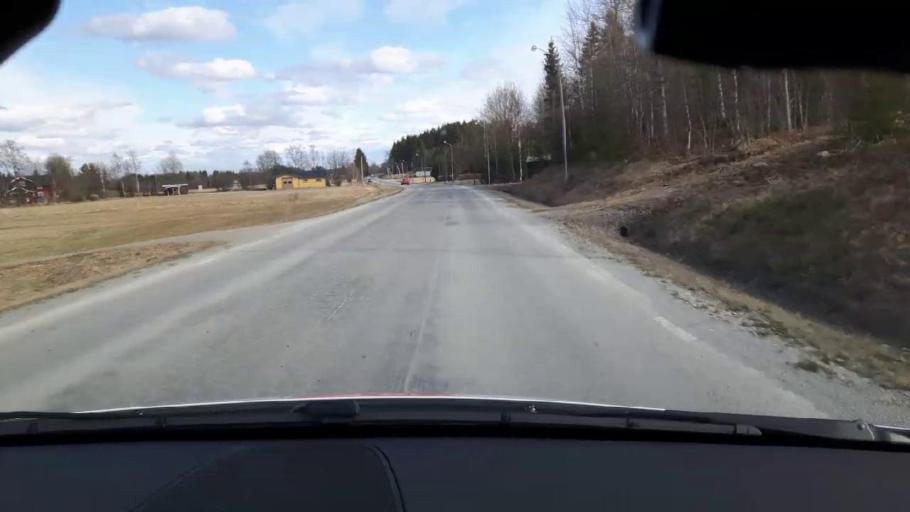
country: SE
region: Jaemtland
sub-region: Bergs Kommun
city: Hoverberg
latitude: 62.7867
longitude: 14.4938
